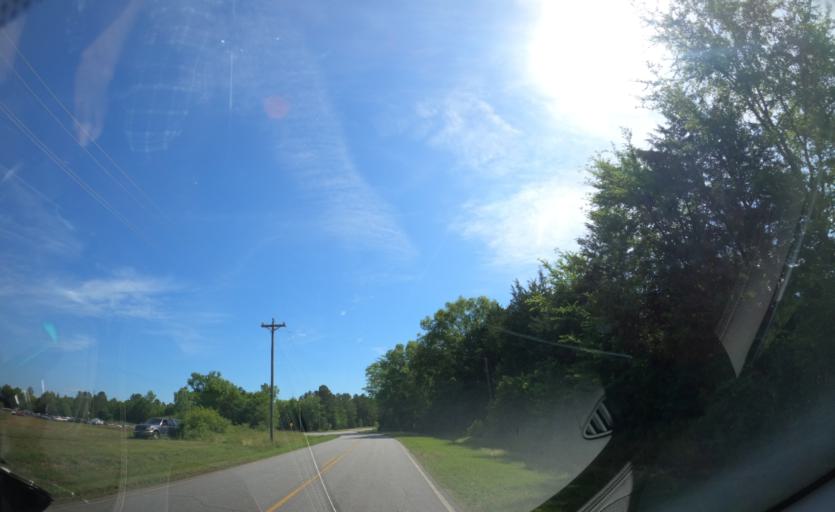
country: US
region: South Carolina
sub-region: Abbeville County
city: Calhoun Falls
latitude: 34.1068
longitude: -82.7238
